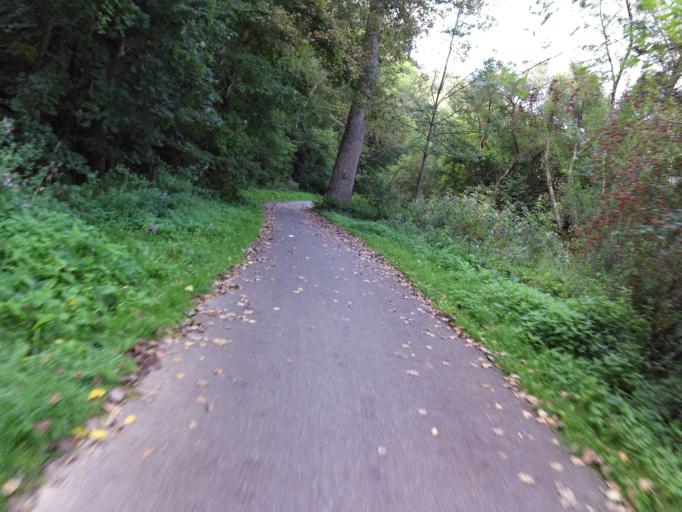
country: DE
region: Baden-Wuerttemberg
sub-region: Karlsruhe Region
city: Horb am Neckar
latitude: 48.4438
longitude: 8.7139
